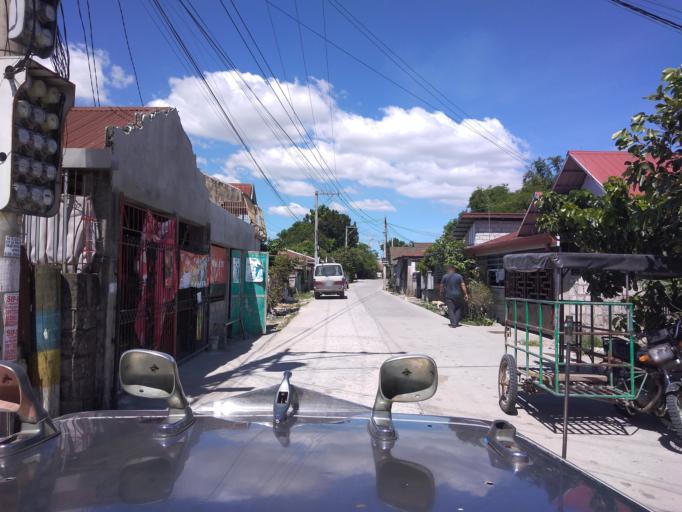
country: PH
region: Central Luzon
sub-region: Province of Pampanga
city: Magliman
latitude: 15.0453
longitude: 120.6432
